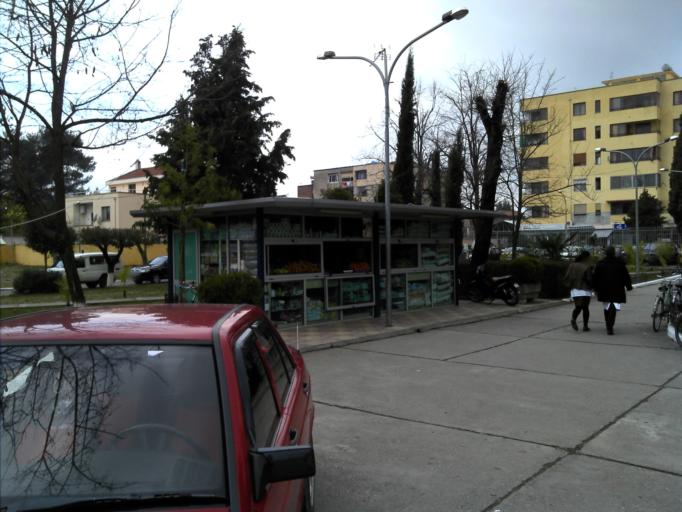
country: AL
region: Shkoder
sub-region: Rrethi i Shkodres
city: Shkoder
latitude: 42.0743
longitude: 19.5242
